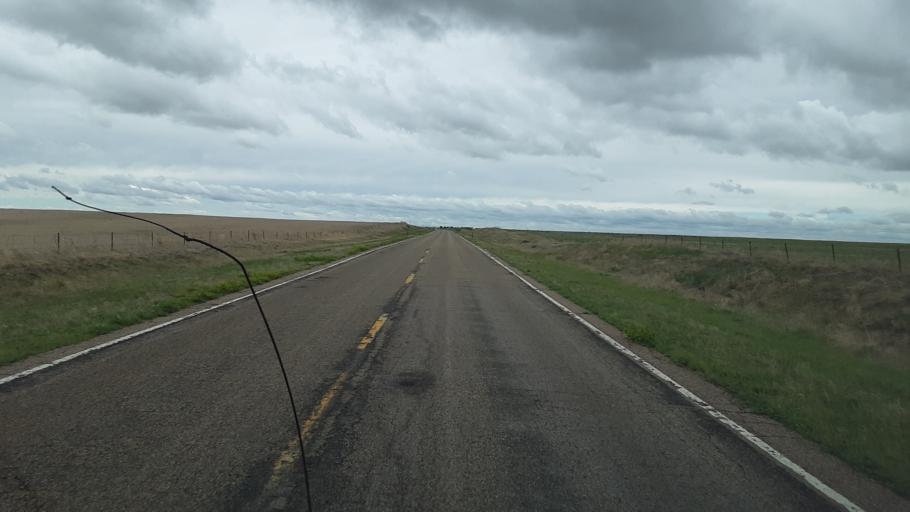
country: US
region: Colorado
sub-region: Lincoln County
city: Hugo
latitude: 38.8517
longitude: -103.6588
